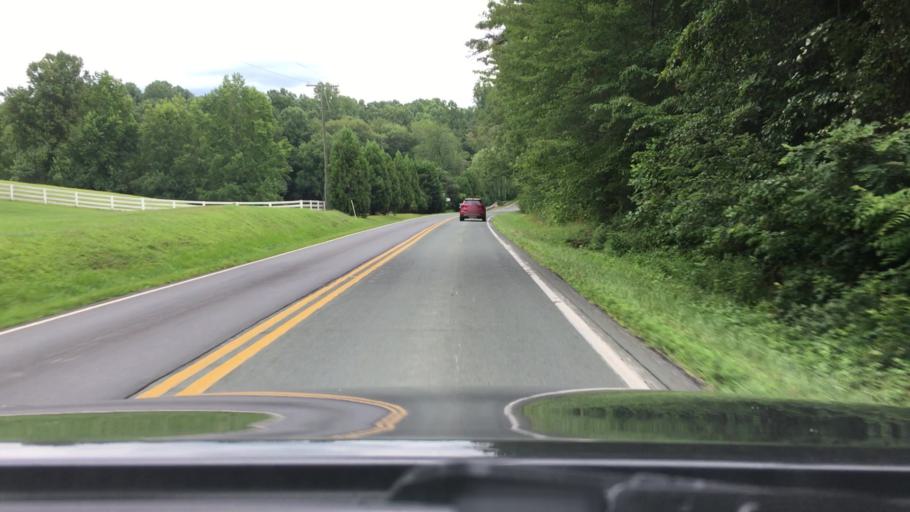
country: US
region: Virginia
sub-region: Orange County
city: Gordonsville
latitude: 38.0899
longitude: -78.2737
